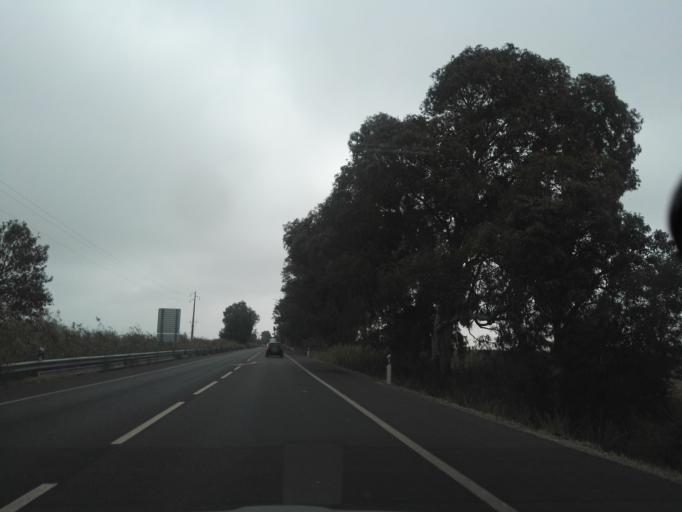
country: PT
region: Lisbon
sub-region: Vila Franca de Xira
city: Vila Franca de Xira
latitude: 38.9500
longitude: -8.9696
